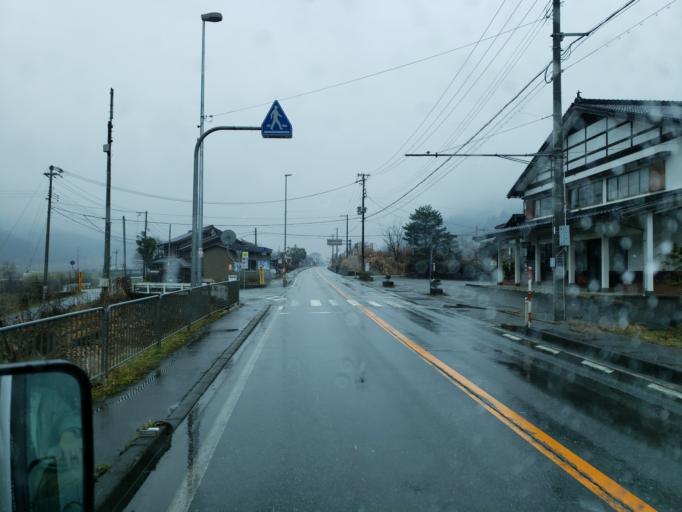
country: JP
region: Hyogo
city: Toyooka
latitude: 35.3863
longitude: 134.7250
